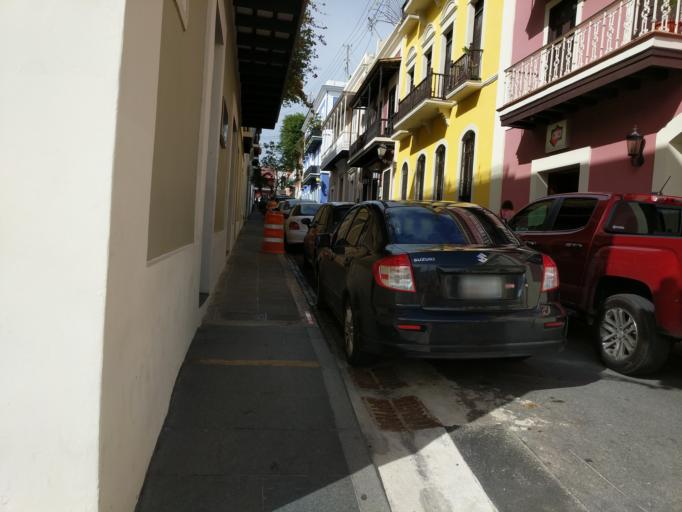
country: PR
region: San Juan
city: San Juan
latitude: 18.4662
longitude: -66.1174
